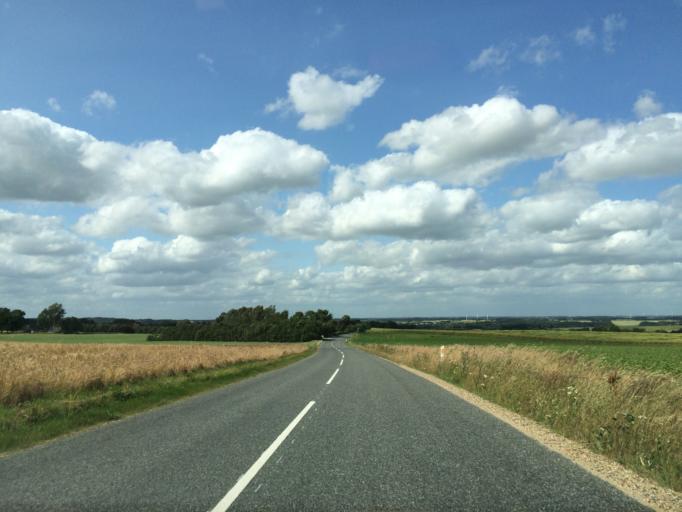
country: DK
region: Central Jutland
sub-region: Skanderborg Kommune
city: Ry
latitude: 56.2022
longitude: 9.7565
